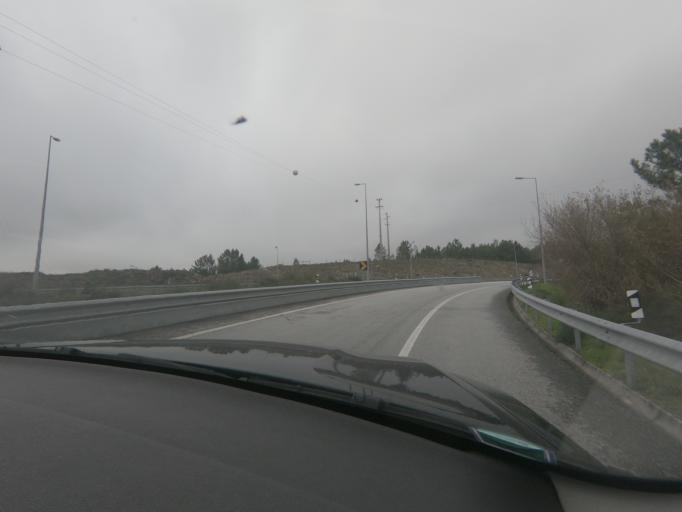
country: PT
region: Viseu
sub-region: Viseu
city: Abraveses
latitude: 40.6729
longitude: -7.9713
